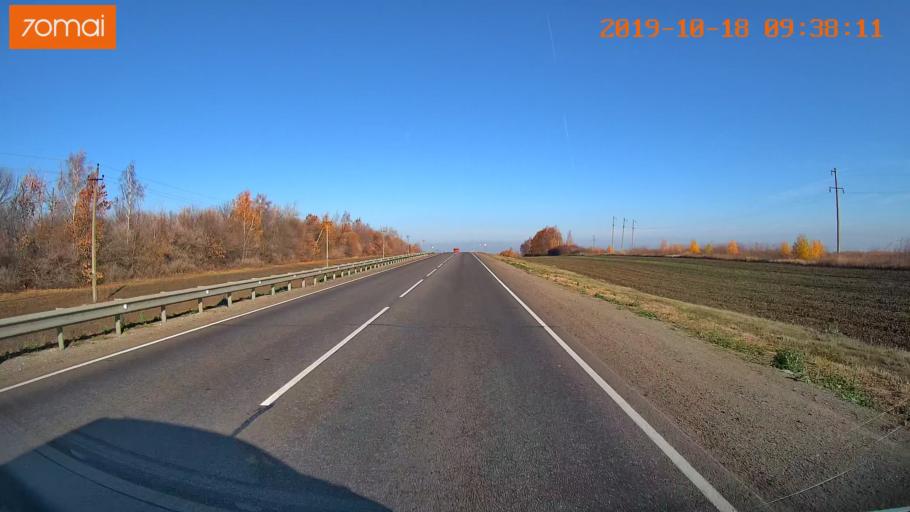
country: RU
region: Tula
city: Yefremov
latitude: 53.2340
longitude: 38.1381
